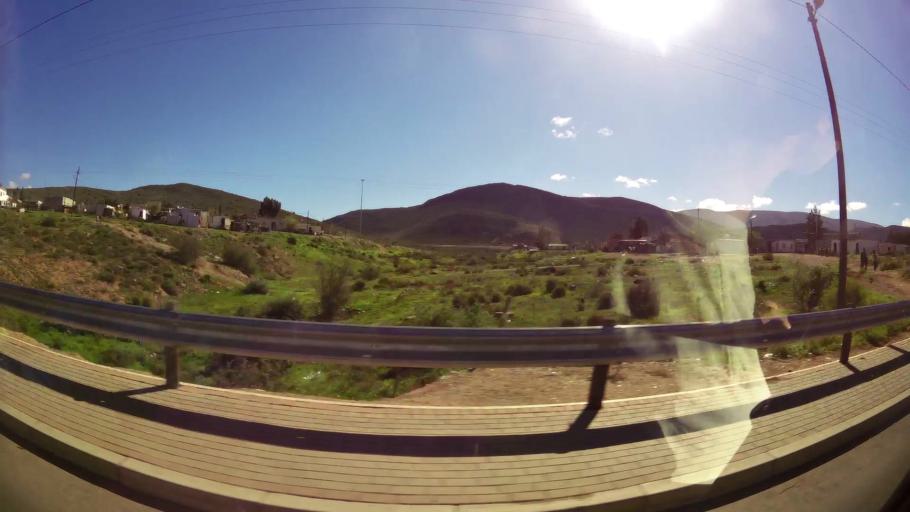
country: ZA
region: Western Cape
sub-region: Cape Winelands District Municipality
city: Ashton
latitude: -33.7695
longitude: 20.1438
